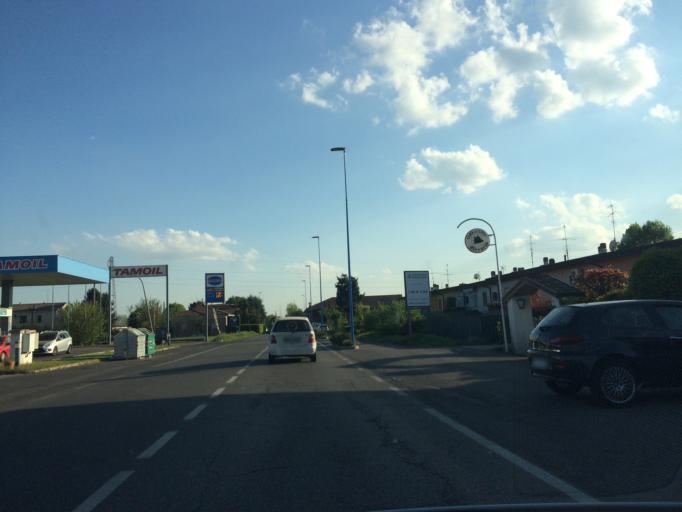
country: IT
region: Lombardy
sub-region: Provincia di Brescia
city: Folzano
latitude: 45.5149
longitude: 10.1946
